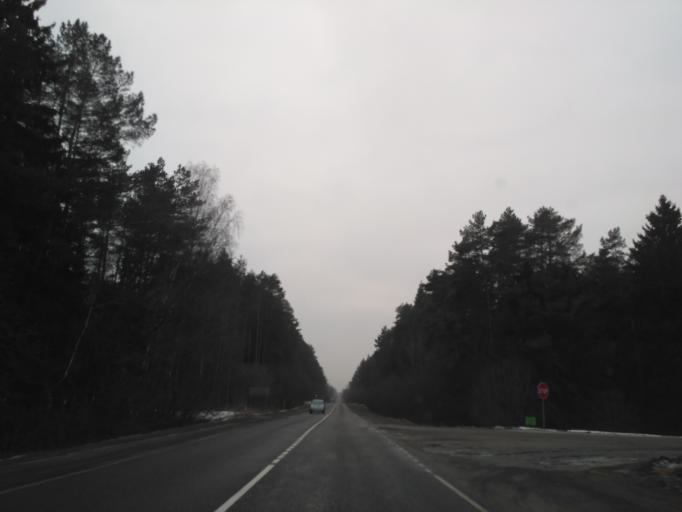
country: BY
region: Minsk
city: Snow
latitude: 53.2813
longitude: 26.3594
